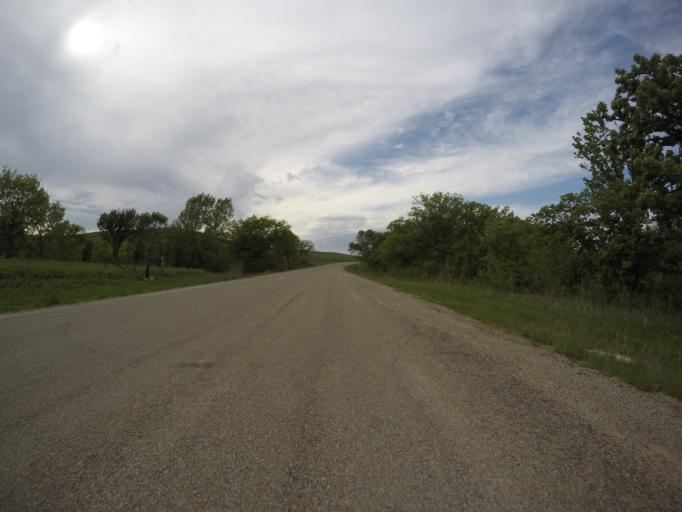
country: US
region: Kansas
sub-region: Riley County
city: Ogden
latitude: 39.0016
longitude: -96.5998
